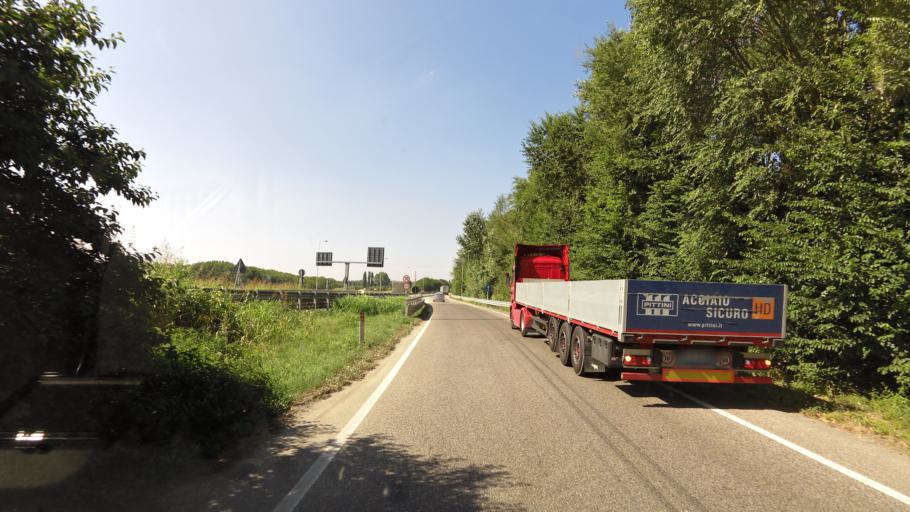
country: IT
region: Emilia-Romagna
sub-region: Provincia di Ravenna
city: Ravenna
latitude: 44.4600
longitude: 12.2090
